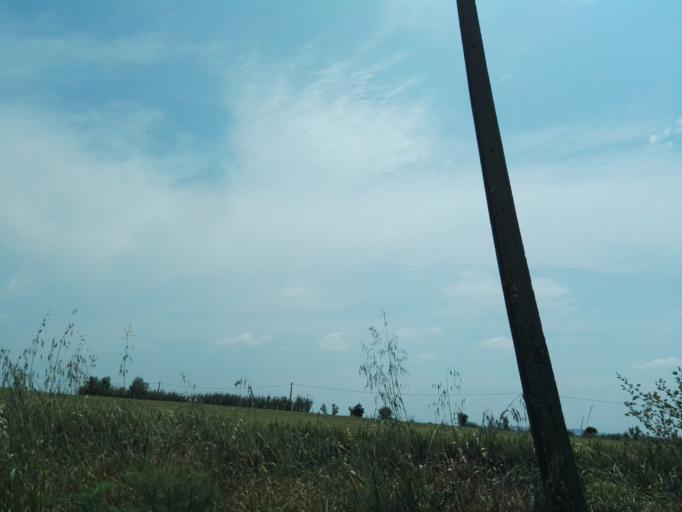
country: PT
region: Santarem
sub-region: Golega
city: Golega
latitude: 39.4186
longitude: -8.4807
